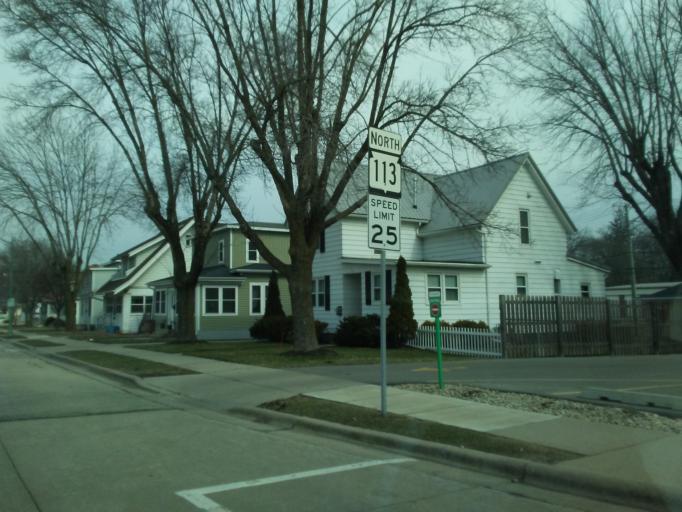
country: US
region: Wisconsin
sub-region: Columbia County
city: Lodi
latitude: 43.3144
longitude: -89.5270
